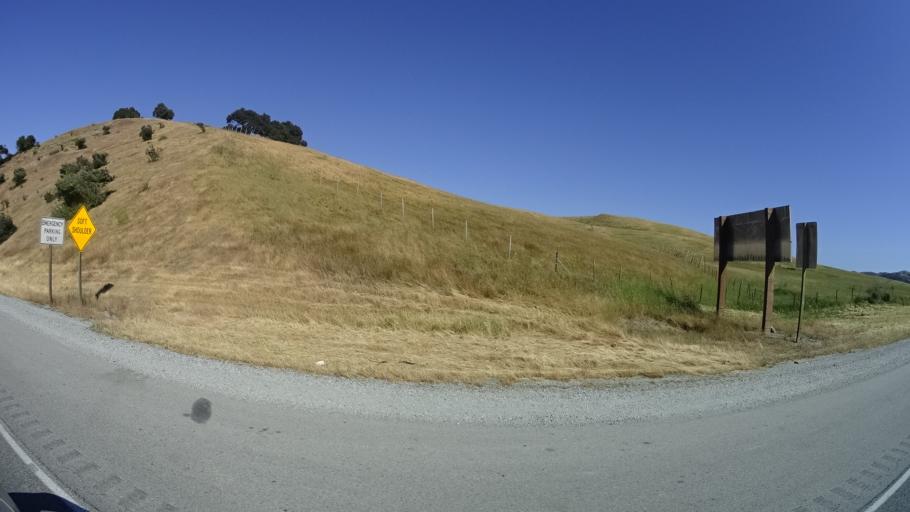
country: US
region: California
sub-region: San Benito County
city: San Juan Bautista
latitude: 36.8656
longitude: -121.5752
